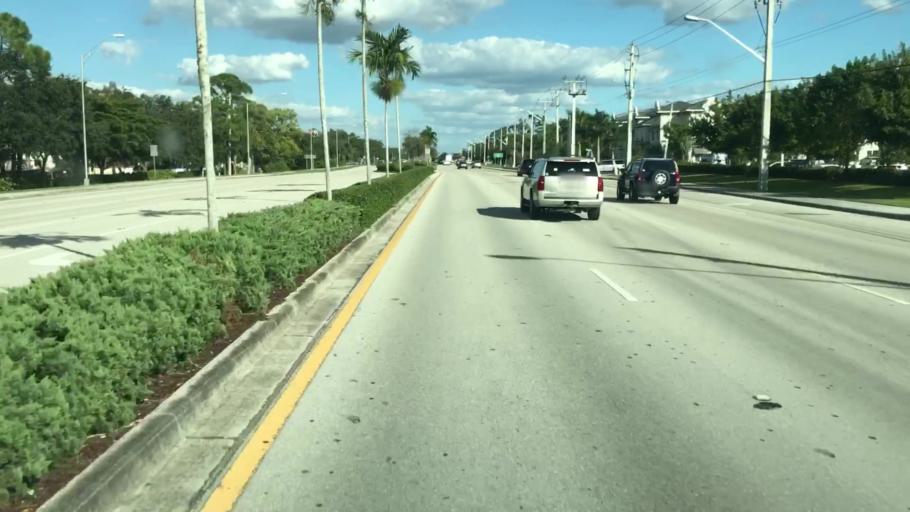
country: US
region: Florida
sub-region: Collier County
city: Naples Park
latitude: 26.2722
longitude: -81.7887
